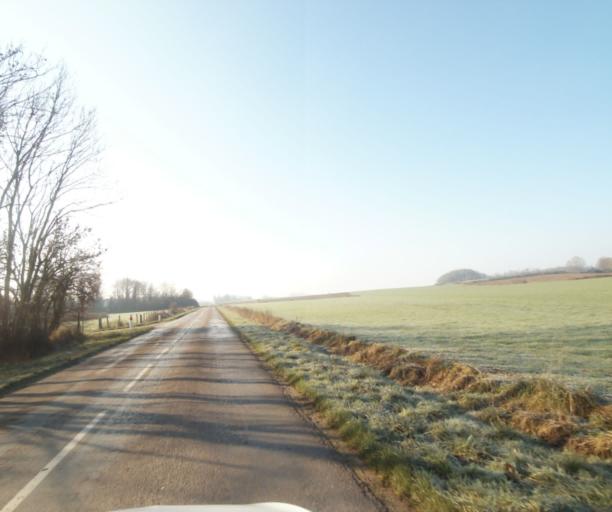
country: FR
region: Champagne-Ardenne
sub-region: Departement de la Haute-Marne
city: Montier-en-Der
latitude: 48.4516
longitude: 4.7666
